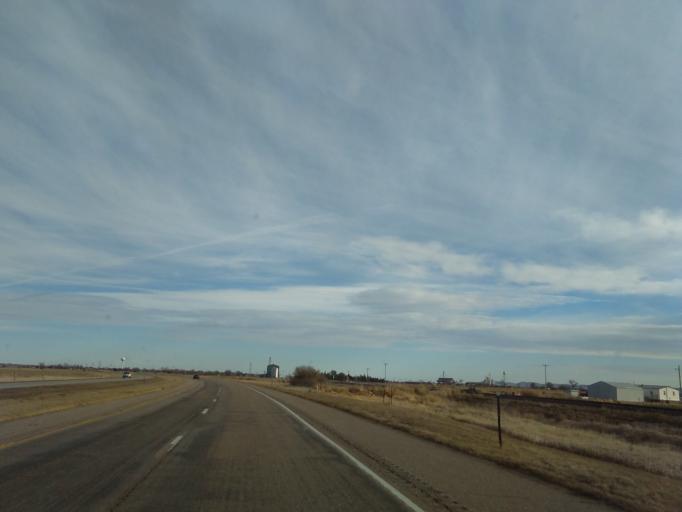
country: US
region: Nebraska
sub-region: Scotts Bluff County
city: Gering
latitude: 41.8166
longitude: -103.5300
